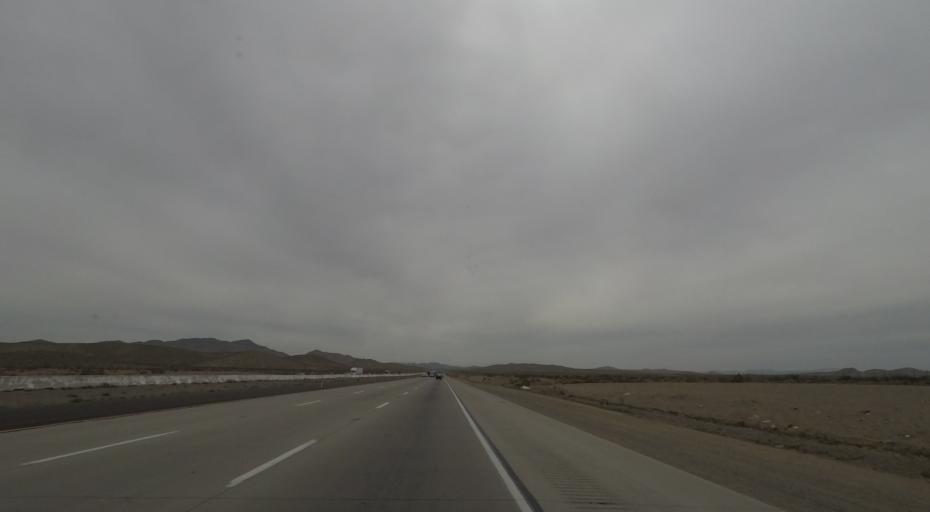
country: US
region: California
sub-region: San Bernardino County
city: Lenwood
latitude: 34.7768
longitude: -117.1379
